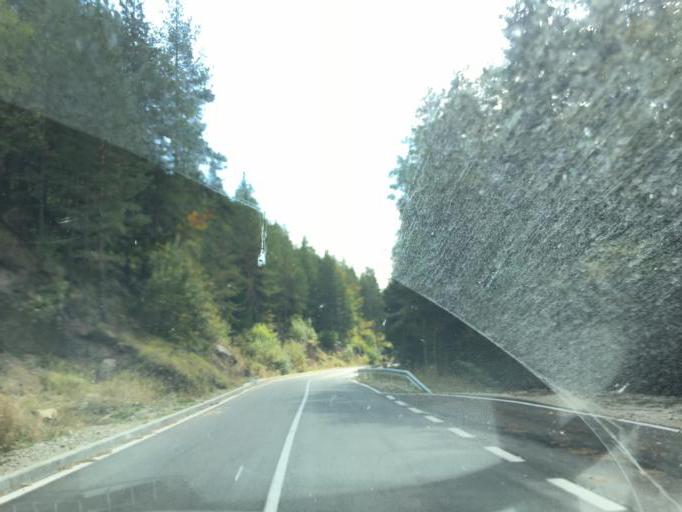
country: BG
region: Pazardzhik
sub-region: Obshtina Batak
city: Batak
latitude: 41.8966
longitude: 24.3197
